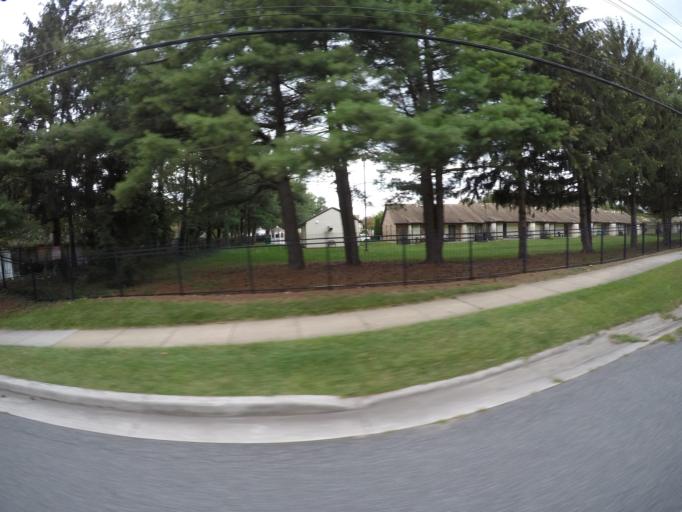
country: US
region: Delaware
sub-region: New Castle County
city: Brookside
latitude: 39.6736
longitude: -75.7284
